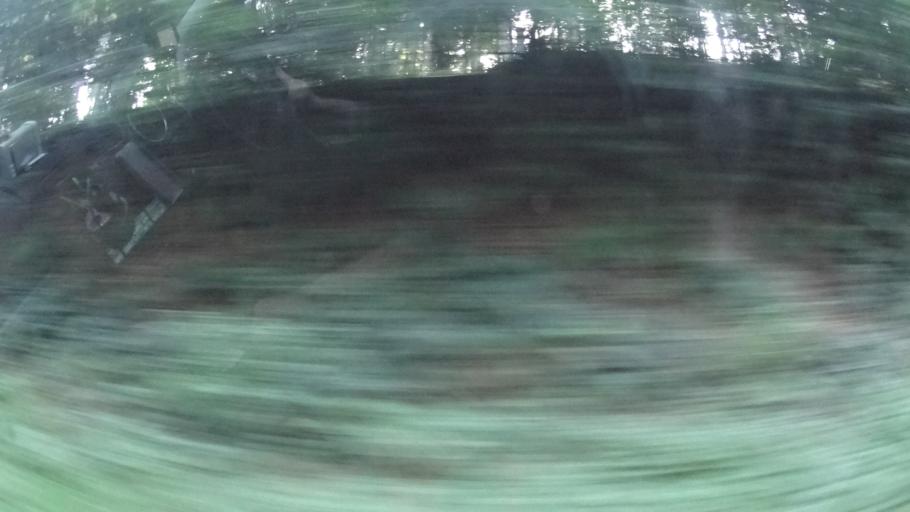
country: DE
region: Hesse
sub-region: Regierungsbezirk Darmstadt
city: Gelnhausen
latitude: 50.2665
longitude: 9.2160
